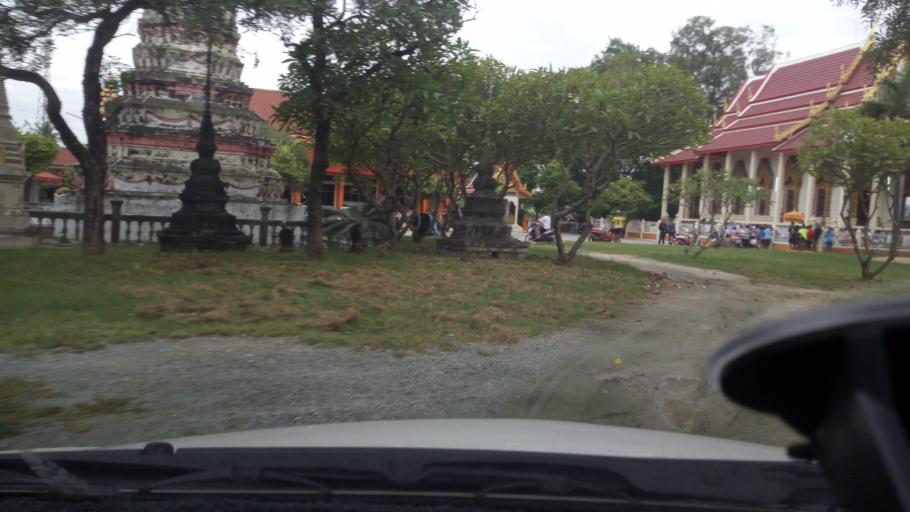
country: TH
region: Chon Buri
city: Ban Bueng
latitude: 13.3638
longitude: 101.0623
